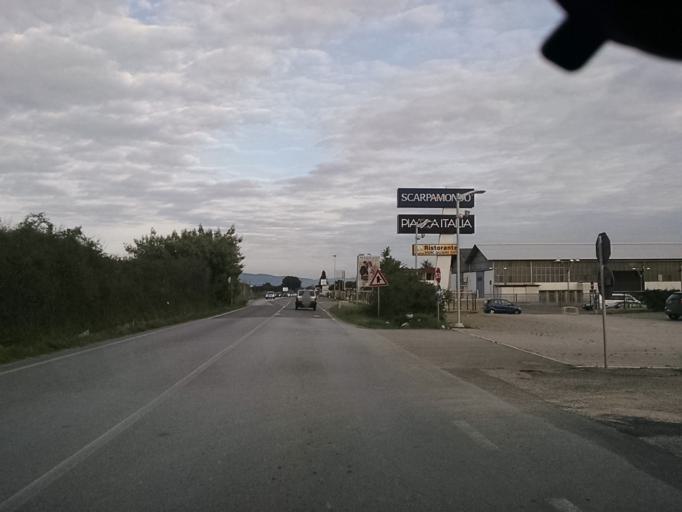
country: IT
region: Tuscany
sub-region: Provincia di Grosseto
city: Follonica
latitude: 42.9364
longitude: 10.7801
